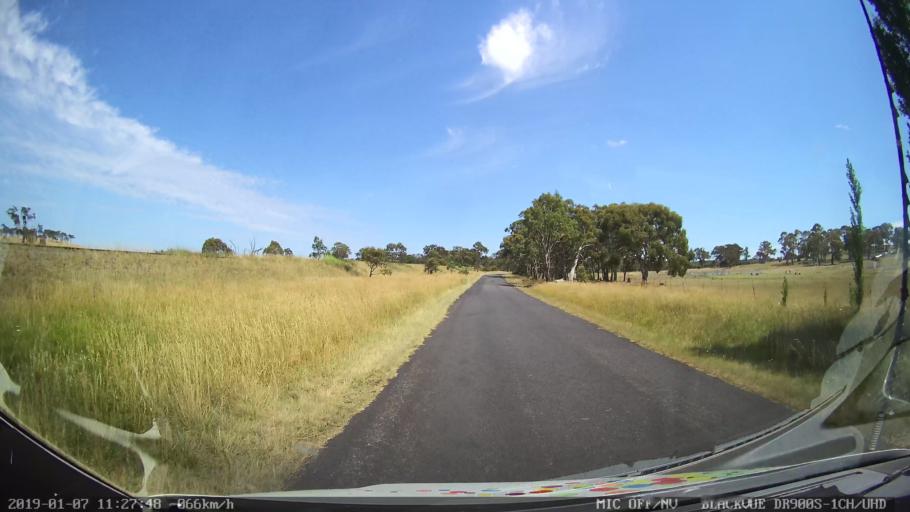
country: AU
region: New South Wales
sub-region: Armidale Dumaresq
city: Armidale
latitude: -30.4544
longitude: 151.5706
